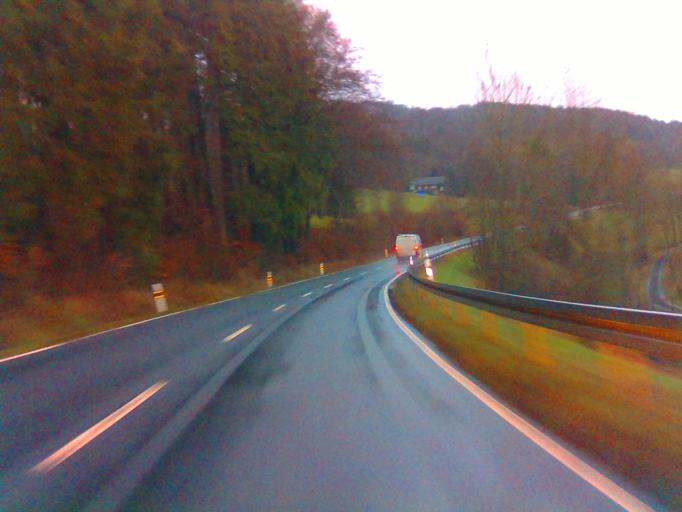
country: DE
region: Hesse
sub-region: Regierungsbezirk Kassel
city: Gersfeld
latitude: 50.4620
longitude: 9.9369
